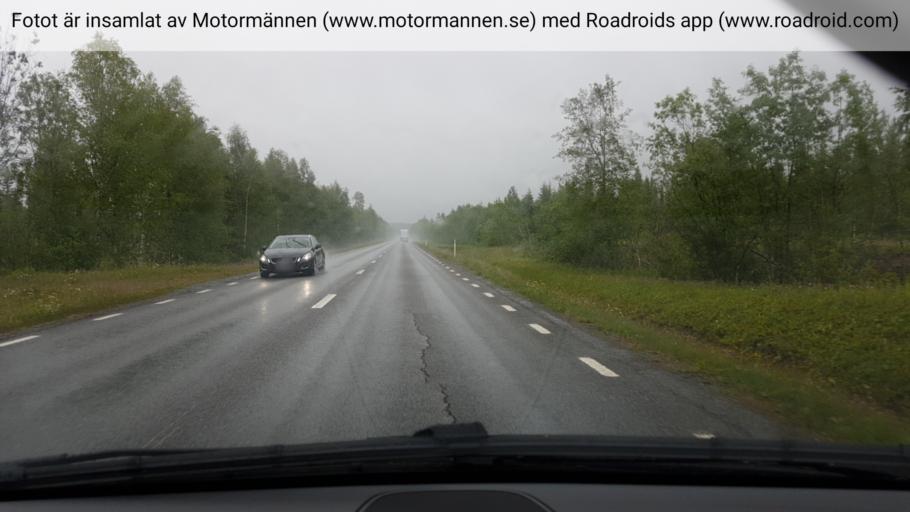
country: SE
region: Jaemtland
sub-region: OEstersunds Kommun
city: Lit
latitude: 63.4418
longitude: 15.1357
